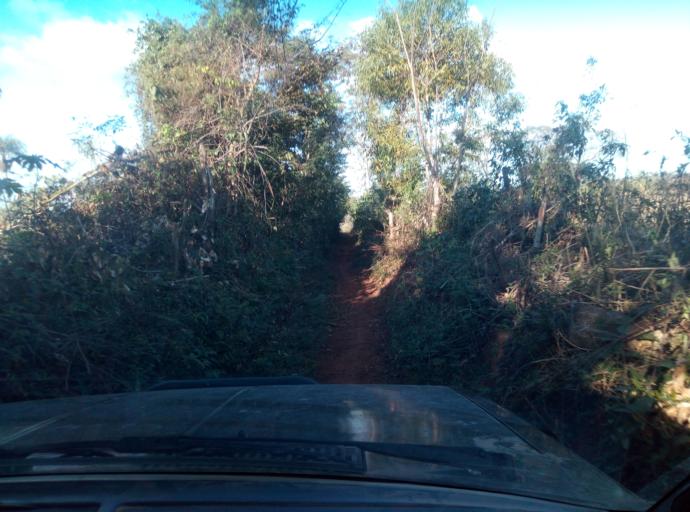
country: PY
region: Caaguazu
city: Carayao
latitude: -25.1756
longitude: -56.2644
